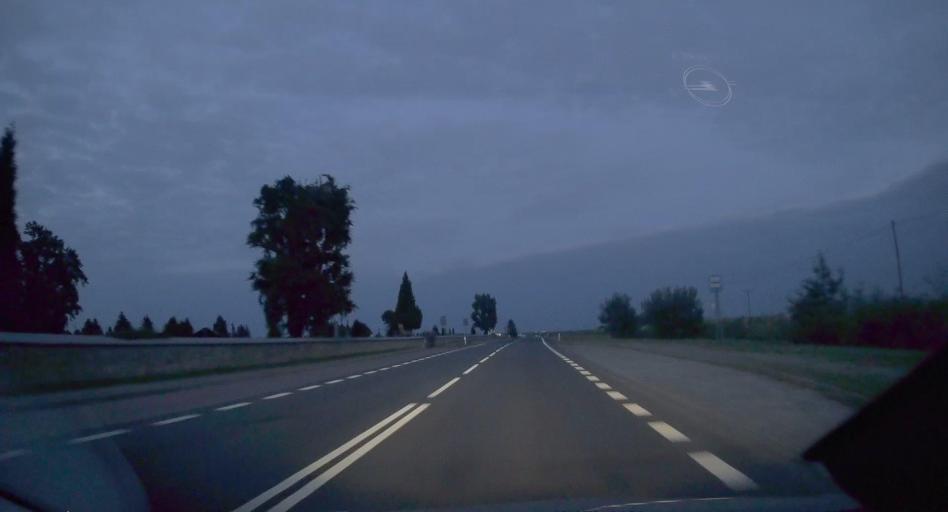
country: PL
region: Silesian Voivodeship
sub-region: Powiat klobucki
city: Klobuck
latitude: 50.8960
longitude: 18.9511
